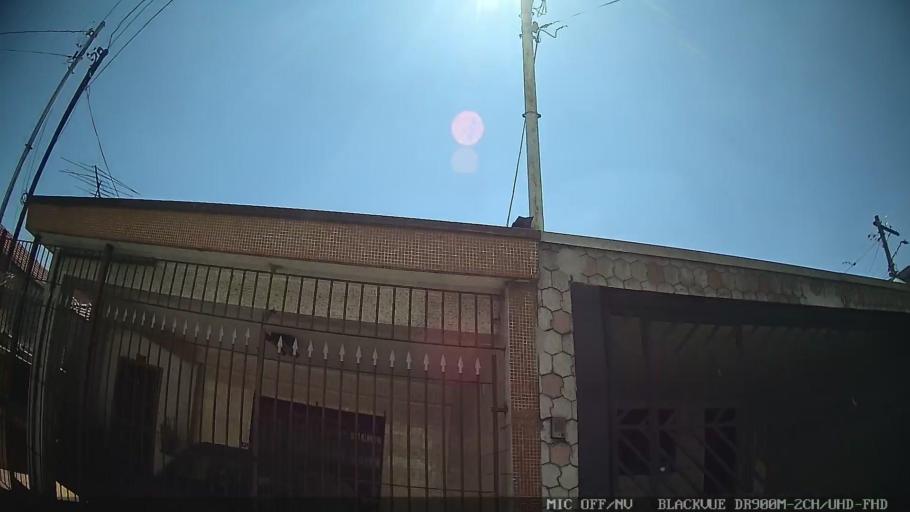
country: BR
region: Sao Paulo
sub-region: Sao Caetano Do Sul
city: Sao Caetano do Sul
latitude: -23.5869
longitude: -46.5431
